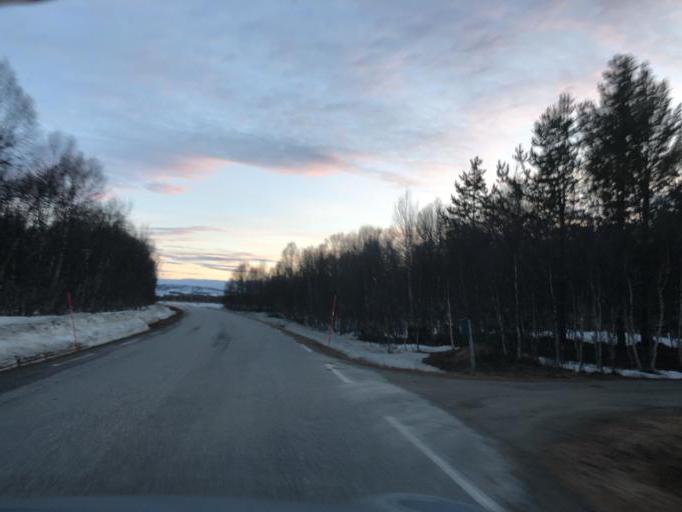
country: NO
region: Sor-Trondelag
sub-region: Tydal
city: Aas
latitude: 62.6782
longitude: 11.8482
